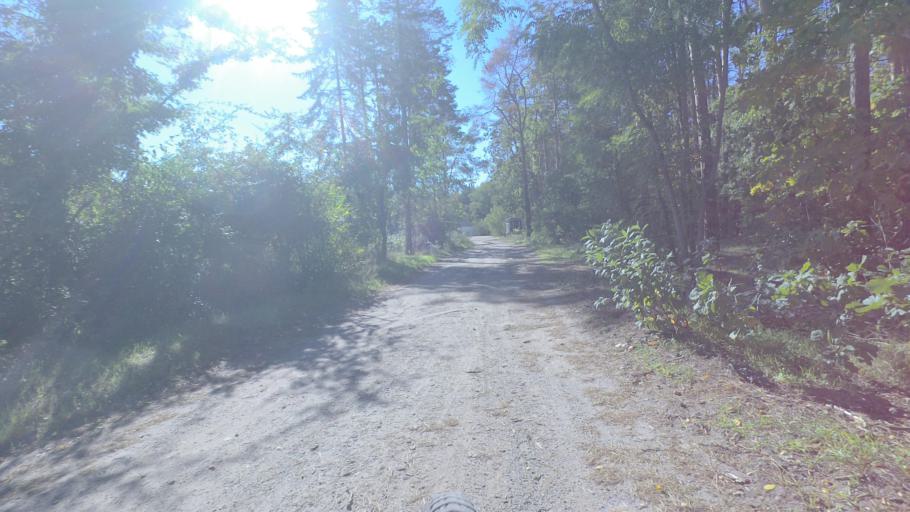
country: DE
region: Brandenburg
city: Am Mellensee
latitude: 52.1748
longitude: 13.3968
